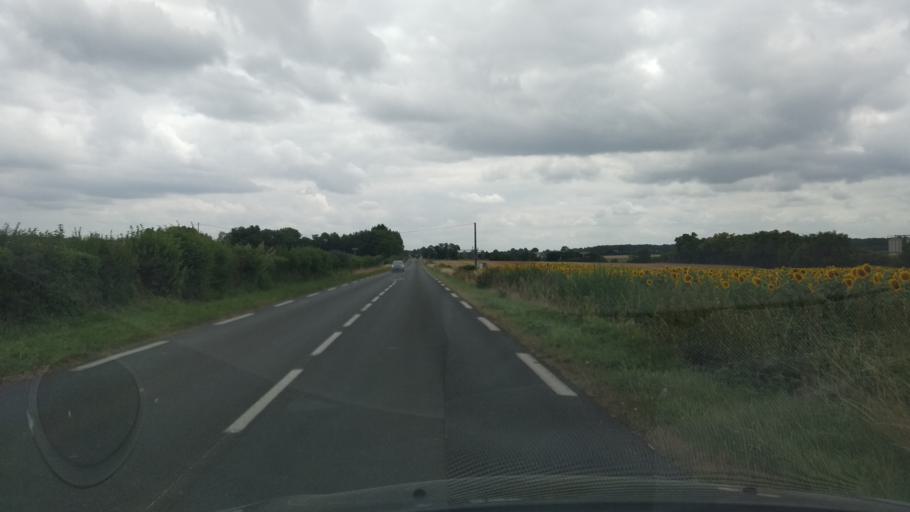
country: FR
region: Poitou-Charentes
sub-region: Departement de la Vienne
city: La Villedieu-du-Clain
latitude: 46.4691
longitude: 0.3681
